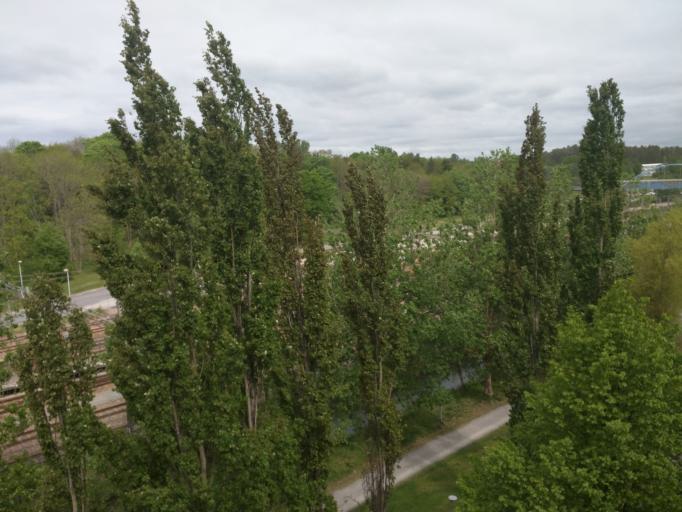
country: SE
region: Stockholm
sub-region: Upplands Vasby Kommun
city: Upplands Vaesby
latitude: 59.5177
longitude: 17.8982
